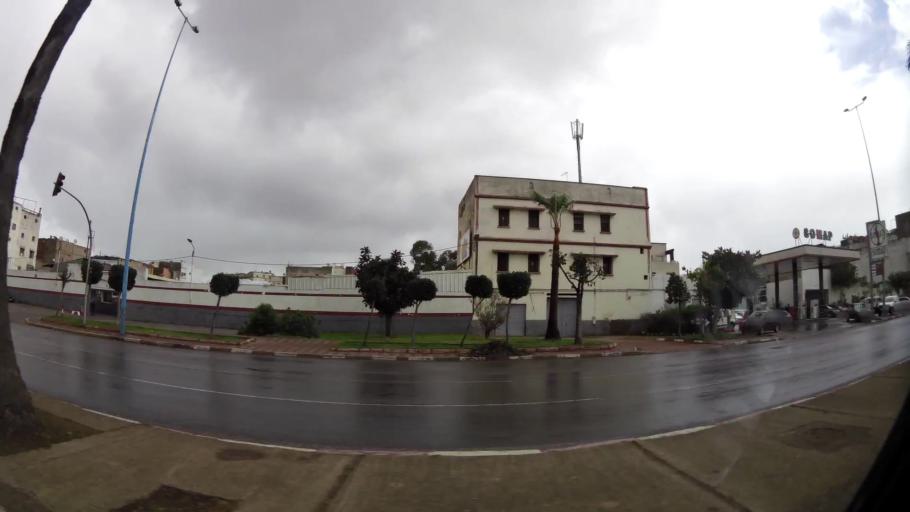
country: MA
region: Grand Casablanca
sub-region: Casablanca
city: Casablanca
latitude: 33.5540
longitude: -7.5916
